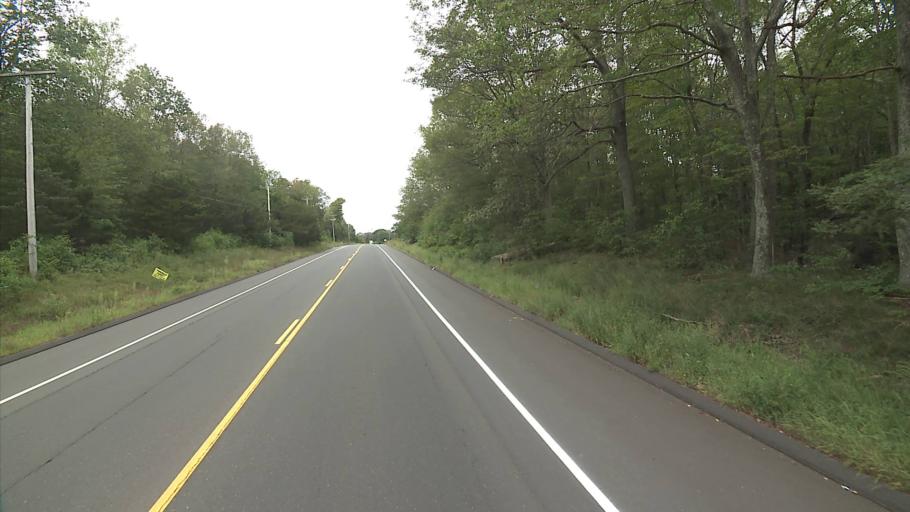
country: US
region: Connecticut
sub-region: New London County
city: Colchester
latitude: 41.5248
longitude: -72.2965
